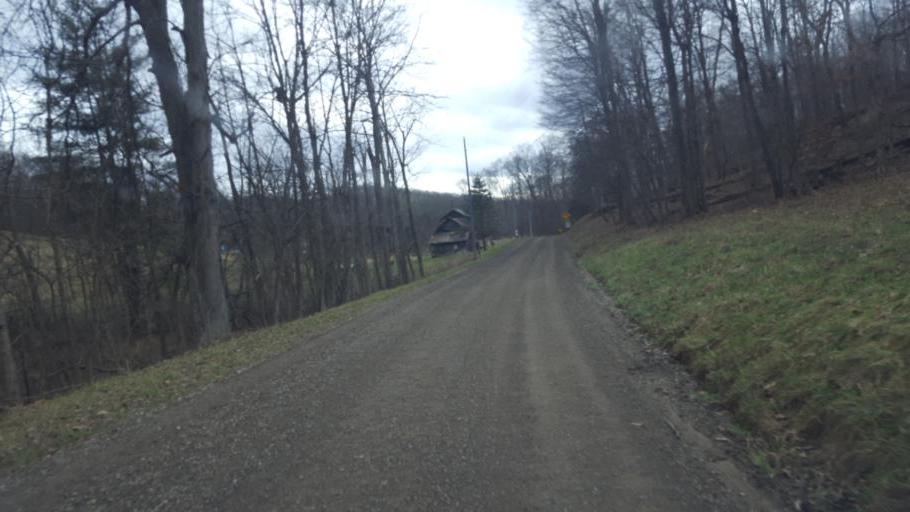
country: US
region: Ohio
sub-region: Licking County
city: Newark
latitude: 40.1724
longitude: -82.3160
